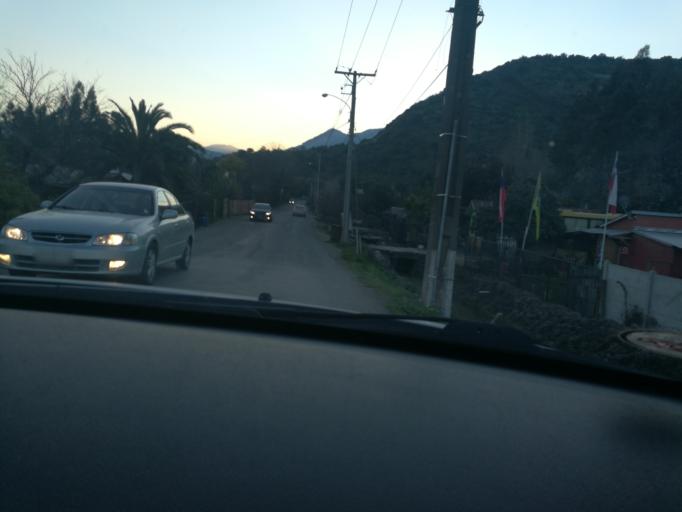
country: CL
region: O'Higgins
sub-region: Provincia de Cachapoal
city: Graneros
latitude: -34.0409
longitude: -70.7204
